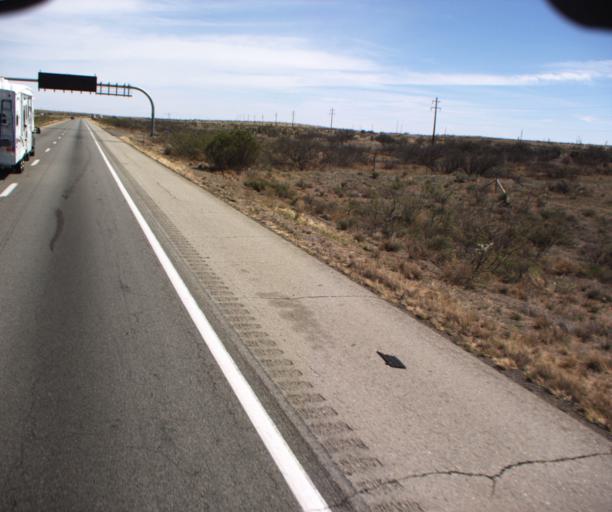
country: US
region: Arizona
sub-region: Cochise County
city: Willcox
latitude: 32.3412
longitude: -109.7545
